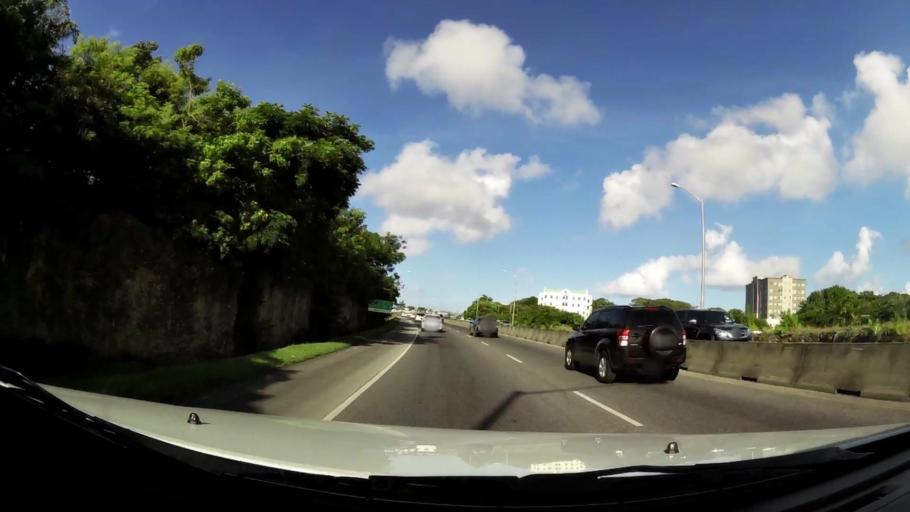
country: BB
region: Saint Michael
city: Bridgetown
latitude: 13.1414
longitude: -59.6042
